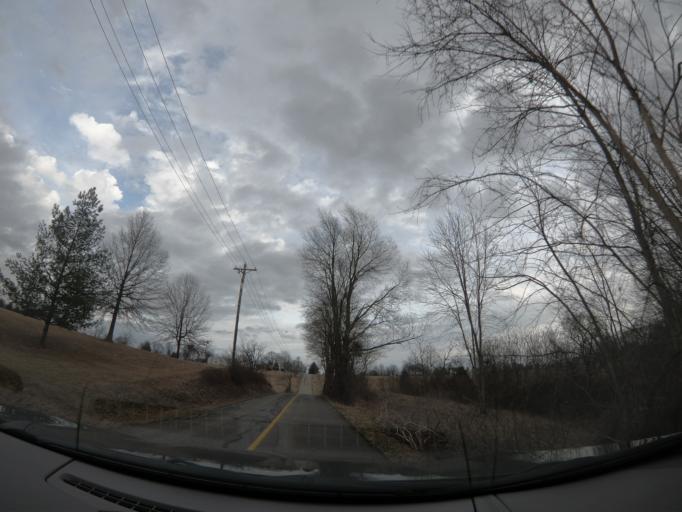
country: US
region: Indiana
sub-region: Floyd County
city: Galena
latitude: 38.3822
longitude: -85.9093
